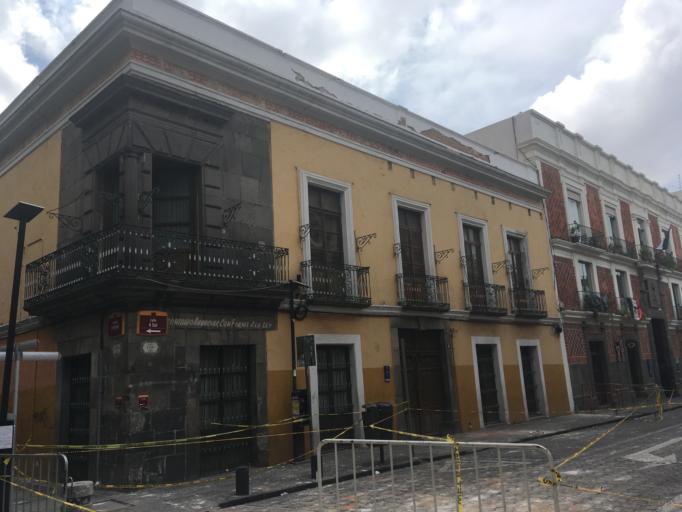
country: MX
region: Puebla
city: Puebla
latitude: 19.0421
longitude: -98.1962
